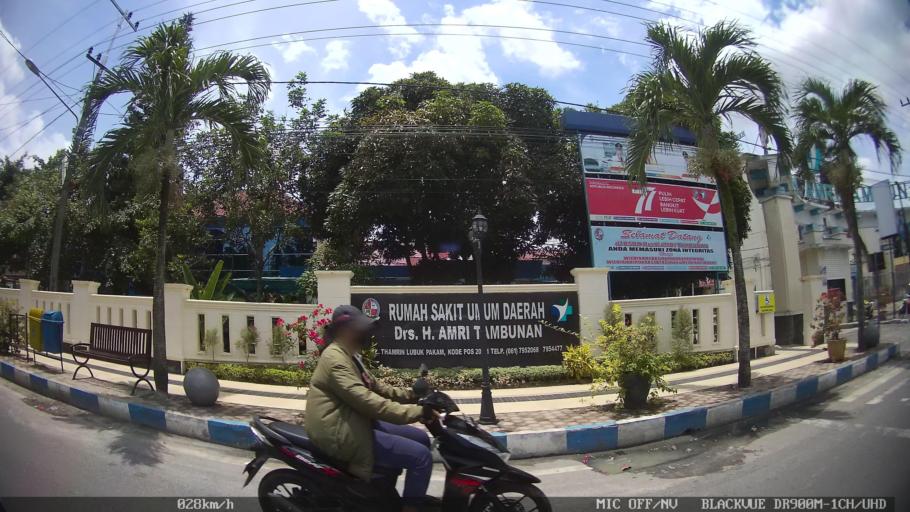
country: ID
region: North Sumatra
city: Percut
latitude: 3.5574
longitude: 98.8679
